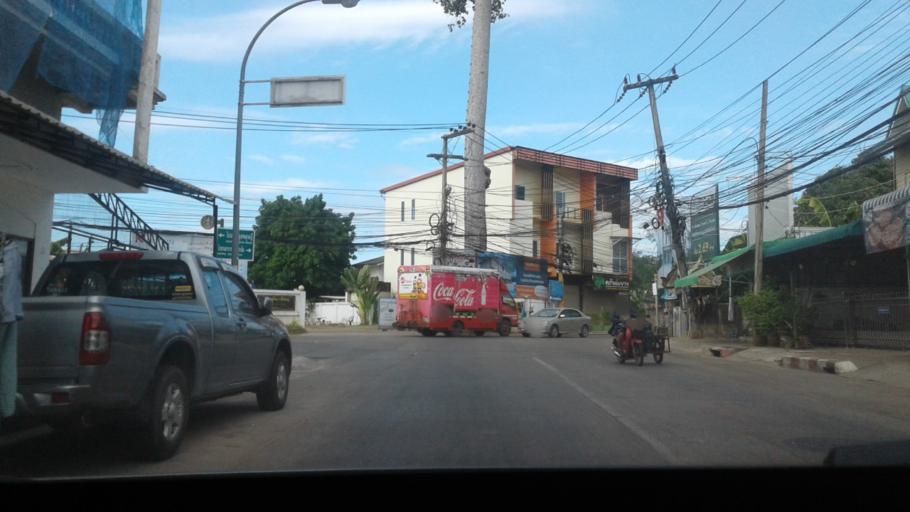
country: TH
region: Changwat Udon Thani
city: Udon Thani
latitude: 17.4172
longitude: 102.8001
